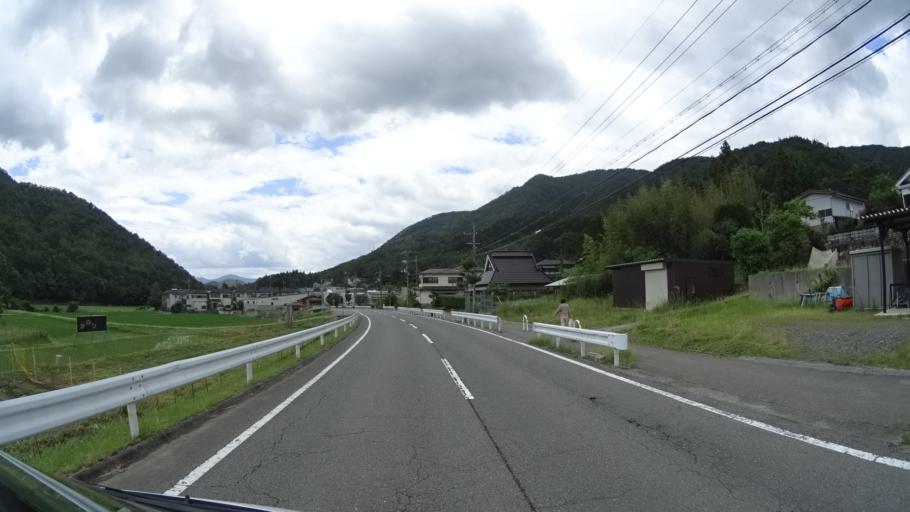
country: JP
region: Kyoto
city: Kameoka
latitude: 35.0116
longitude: 135.4306
